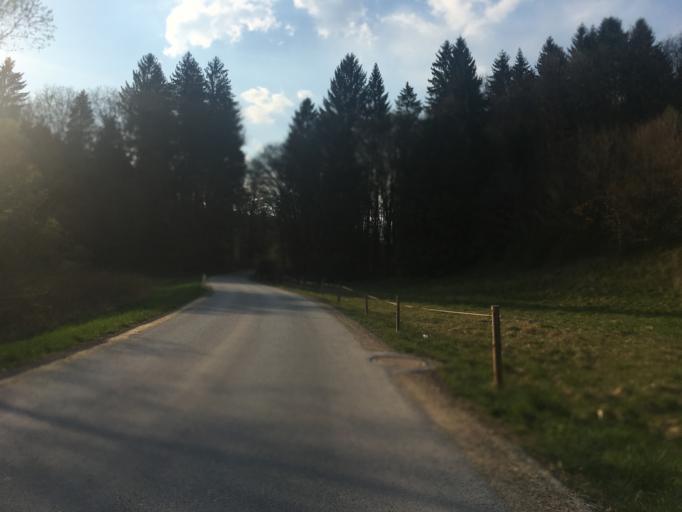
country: AT
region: Styria
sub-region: Politischer Bezirk Graz-Umgebung
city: Nestelbach bei Graz
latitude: 47.0784
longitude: 15.6323
